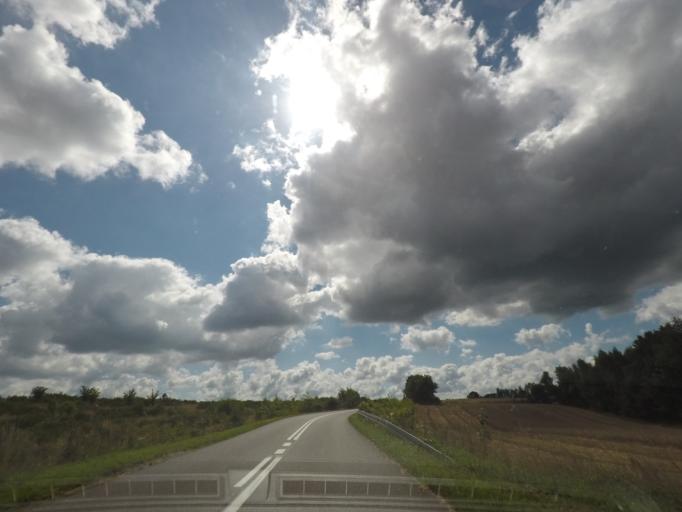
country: PL
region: Pomeranian Voivodeship
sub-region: Powiat wejherowski
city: Leczyce
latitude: 54.6009
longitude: 17.8429
